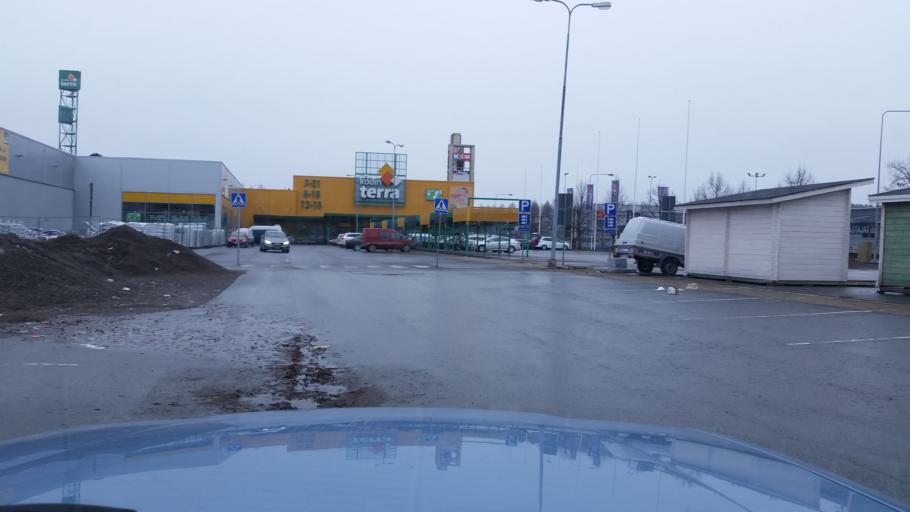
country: FI
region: Haeme
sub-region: Haemeenlinna
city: Haemeenlinna
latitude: 61.0083
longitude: 24.4182
